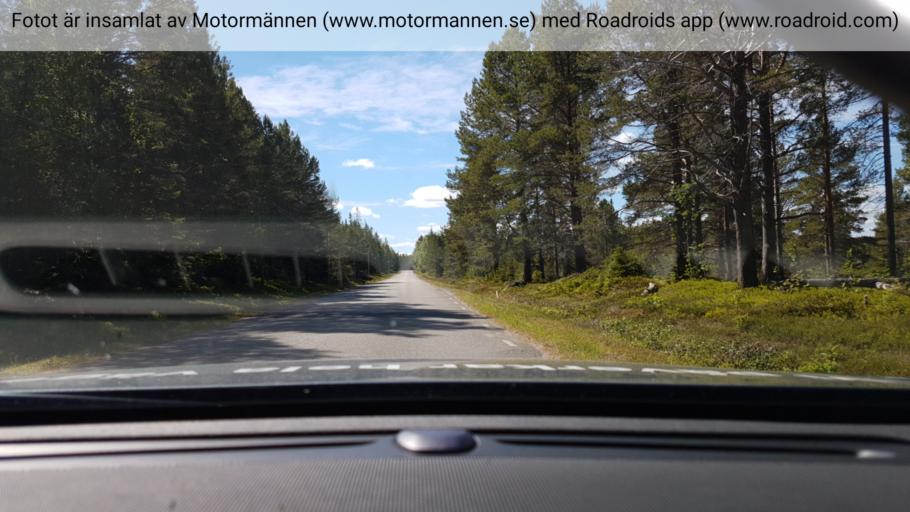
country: SE
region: Vaesterbotten
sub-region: Skelleftea Kommun
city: Burea
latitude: 64.4612
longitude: 21.5850
